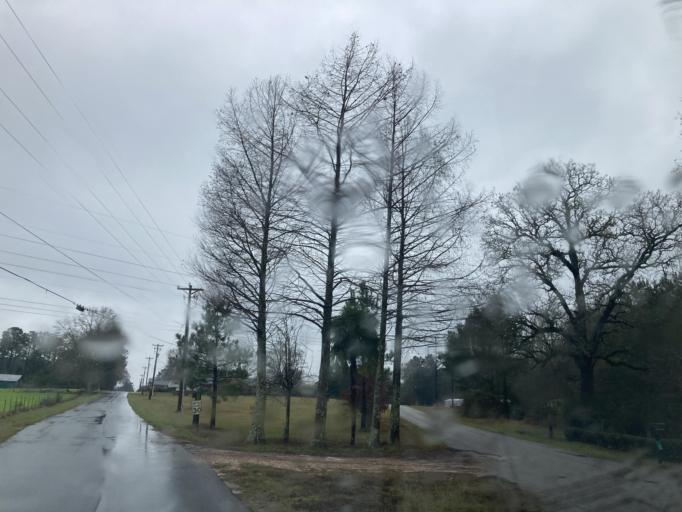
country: US
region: Mississippi
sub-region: Forrest County
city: Rawls Springs
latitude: 31.4873
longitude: -89.3824
